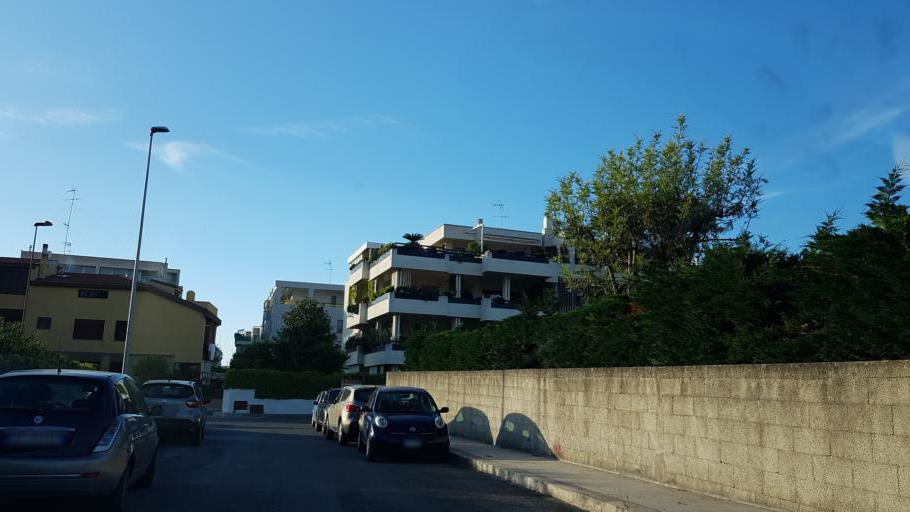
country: IT
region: Apulia
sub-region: Provincia di Brindisi
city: Materdomini
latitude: 40.6458
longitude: 17.9477
